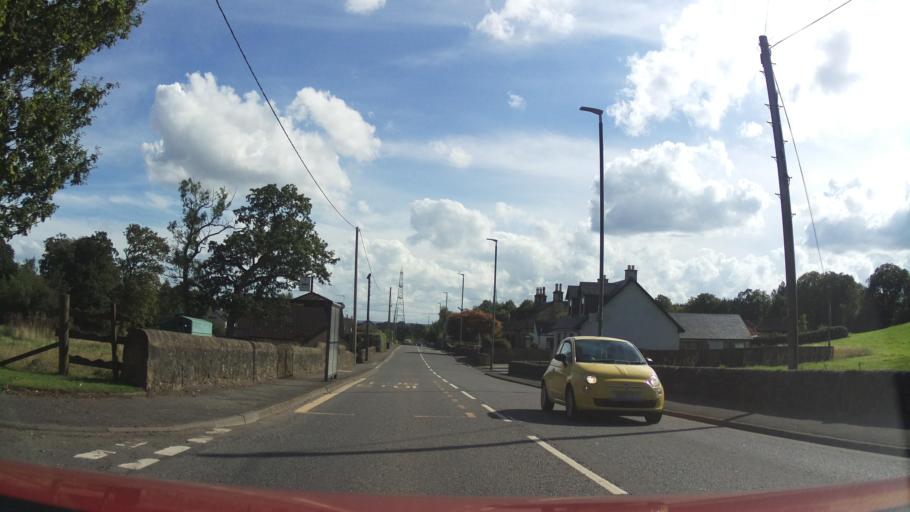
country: GB
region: Scotland
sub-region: Stirling
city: Cowie
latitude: 56.0593
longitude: -3.8699
